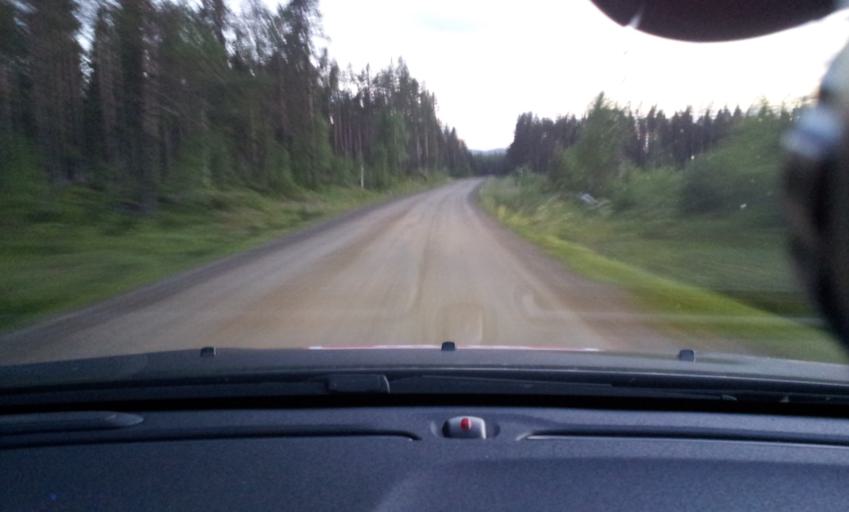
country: SE
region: Vaesternorrland
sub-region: Ange Kommun
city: Ange
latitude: 62.7675
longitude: 15.8243
